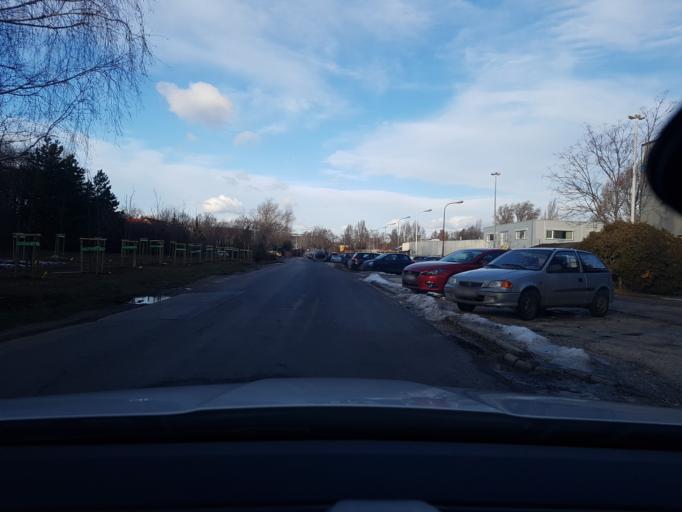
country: HU
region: Budapest
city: Budapest III. keruelet
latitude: 47.5589
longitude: 19.0295
